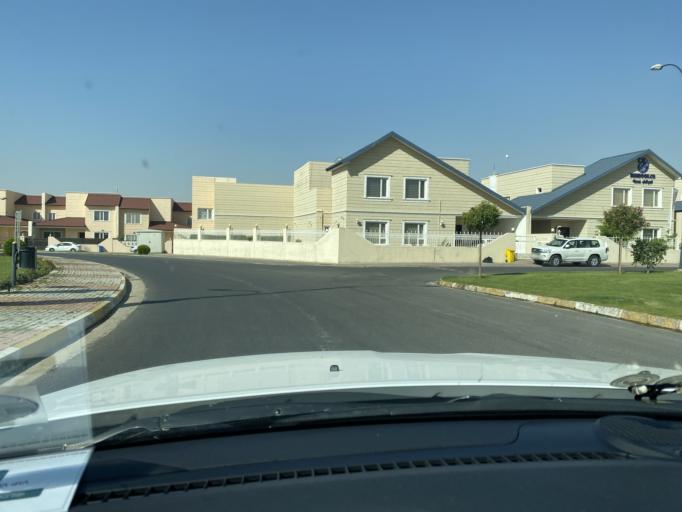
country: IQ
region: Arbil
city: Erbil
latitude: 36.2419
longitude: 44.0508
